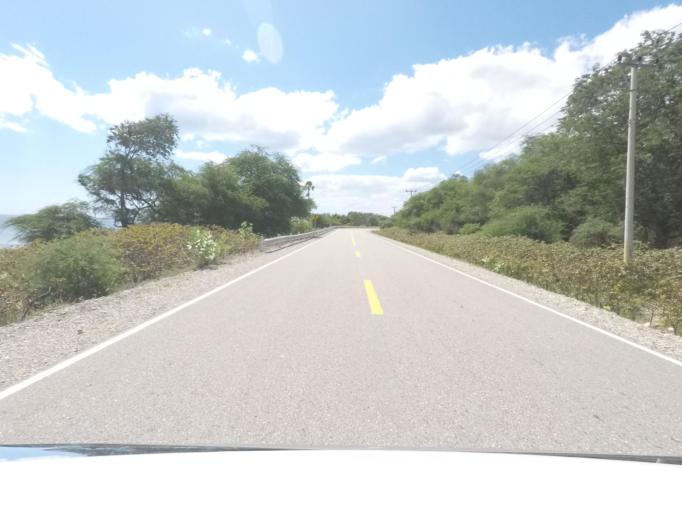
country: TL
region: Baucau
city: Baucau
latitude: -8.4266
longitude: 126.6936
